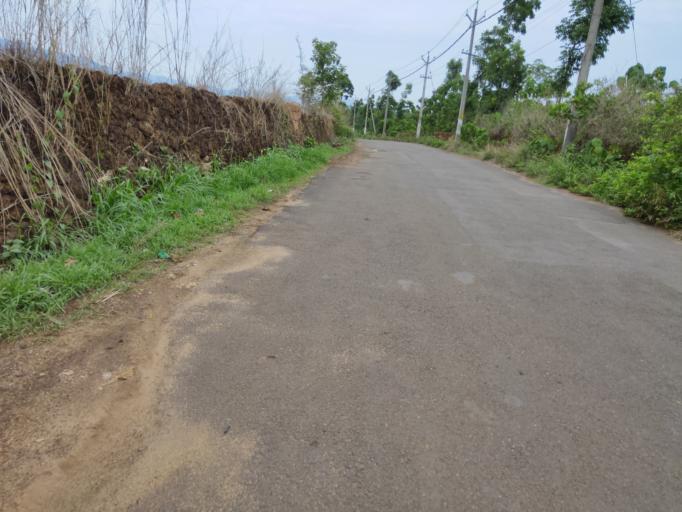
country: IN
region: Kerala
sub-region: Malappuram
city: Manjeri
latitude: 11.2490
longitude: 76.2468
